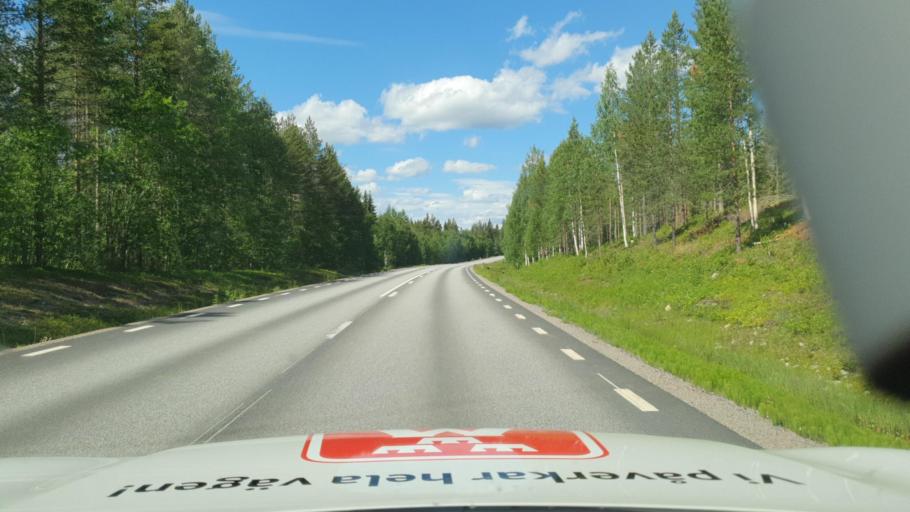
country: SE
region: Vaesterbotten
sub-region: Skelleftea Kommun
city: Boliden
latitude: 64.9052
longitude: 20.3519
